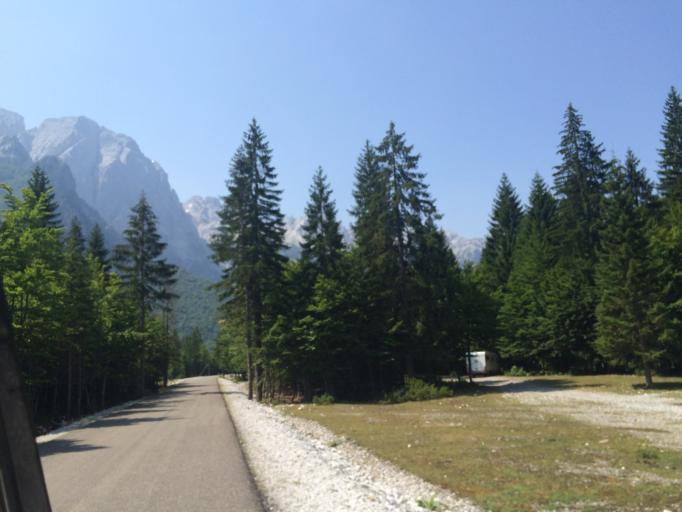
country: AL
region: Kukes
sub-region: Rrethi i Tropojes
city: Valbone
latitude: 42.4293
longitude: 19.8728
